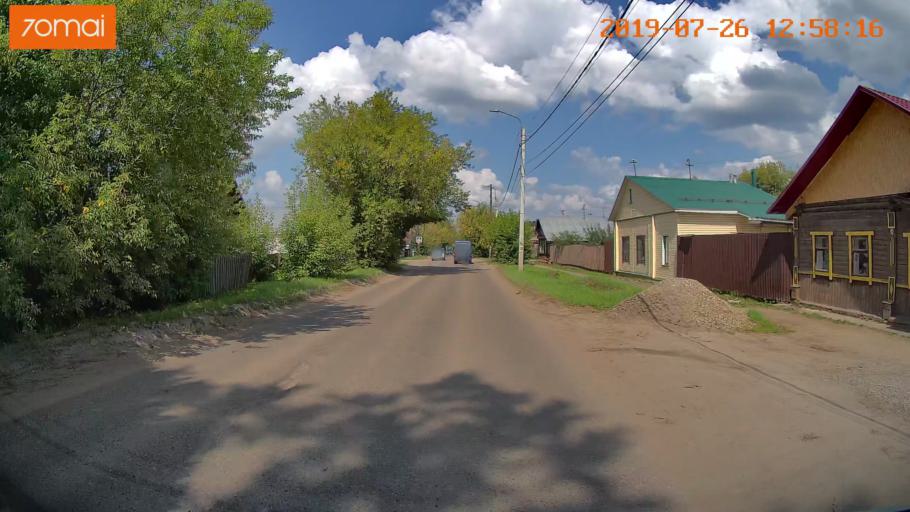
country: RU
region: Ivanovo
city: Bogorodskoye
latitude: 57.0230
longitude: 41.0208
